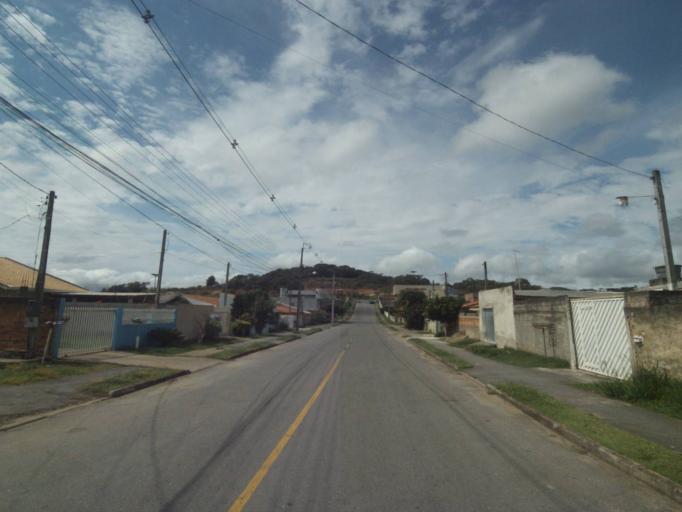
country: BR
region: Parana
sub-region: Quatro Barras
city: Quatro Barras
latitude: -25.3448
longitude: -49.0759
